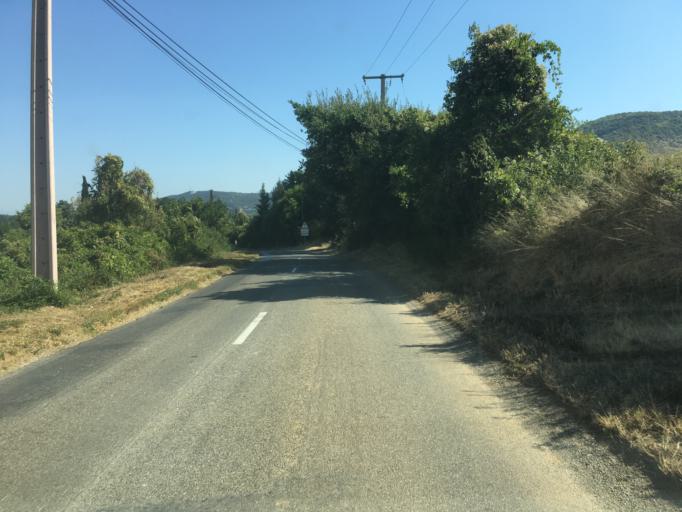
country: FR
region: Provence-Alpes-Cote d'Azur
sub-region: Departement des Alpes-de-Haute-Provence
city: Villeneuve
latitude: 43.8689
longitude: 5.8998
